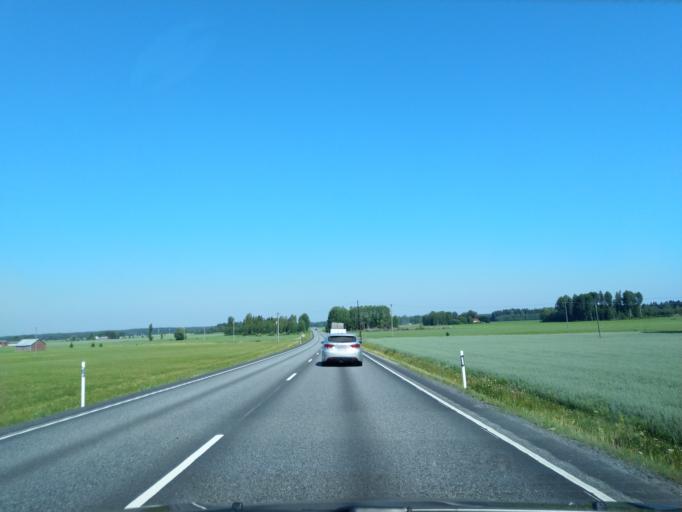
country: FI
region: Varsinais-Suomi
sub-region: Loimaa
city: Alastaro
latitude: 61.0834
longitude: 22.8979
